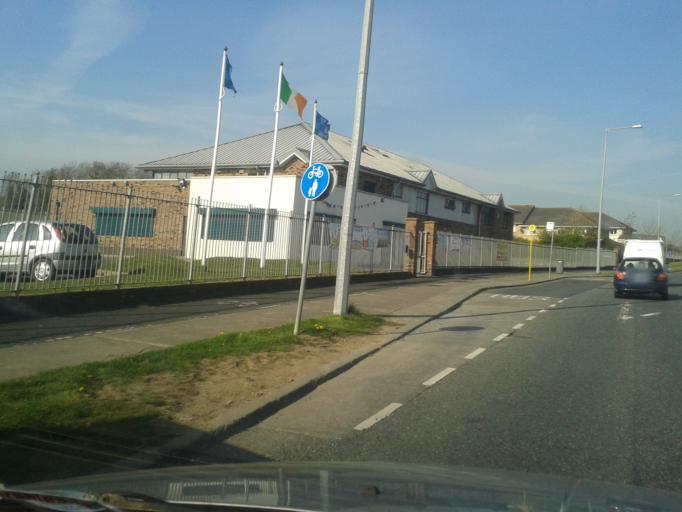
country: IE
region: Leinster
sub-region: Fingal County
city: Swords
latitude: 53.4681
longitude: -6.2209
